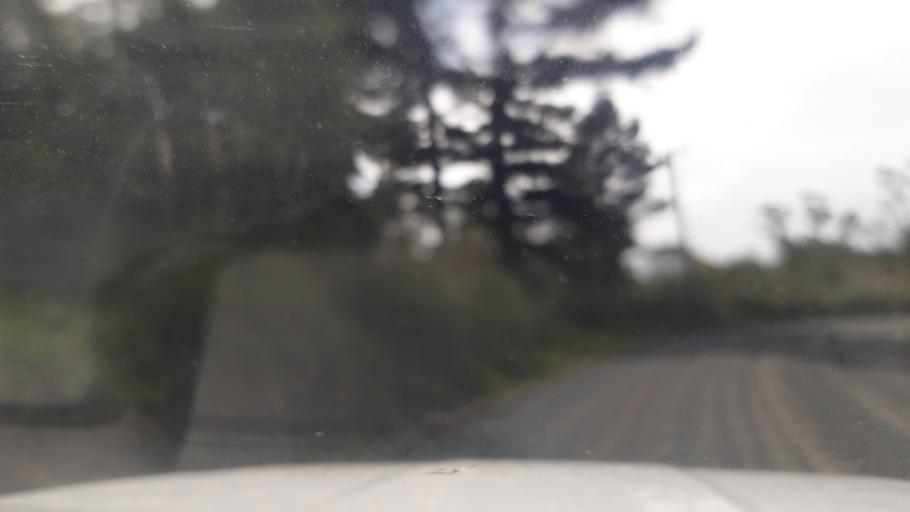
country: NZ
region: Northland
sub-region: Far North District
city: Kaitaia
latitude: -34.8358
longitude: 173.1214
